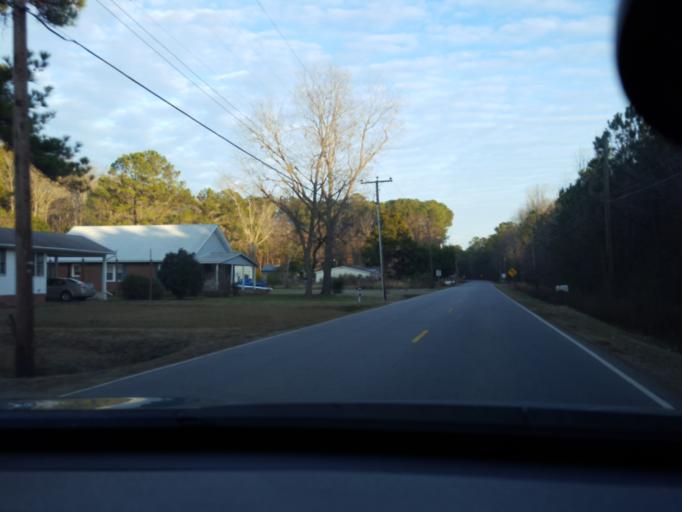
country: US
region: North Carolina
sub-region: Northampton County
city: Jackson
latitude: 36.2704
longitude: -77.2691
